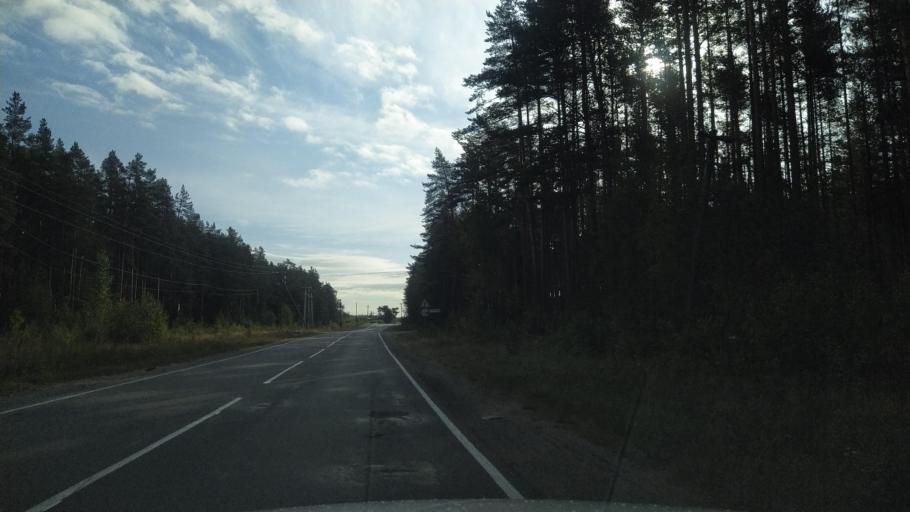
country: RU
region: Leningrad
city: Priozersk
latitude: 61.0038
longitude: 30.2135
